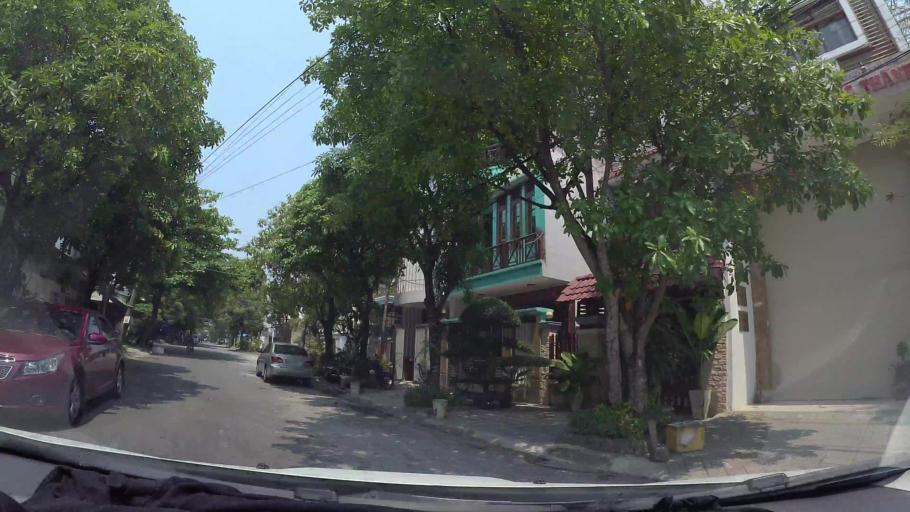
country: VN
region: Da Nang
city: Cam Le
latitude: 16.0166
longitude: 108.2100
